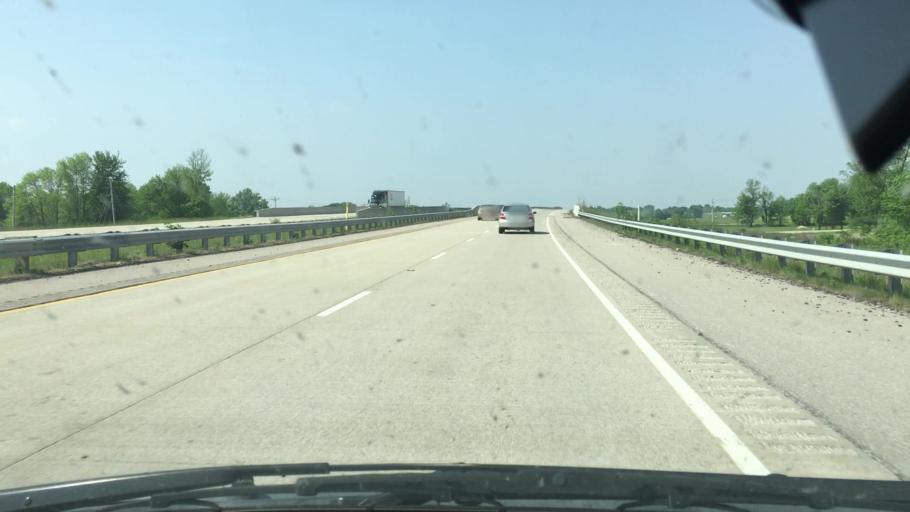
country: US
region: Indiana
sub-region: Daviess County
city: Washington
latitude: 38.6349
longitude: -87.1289
